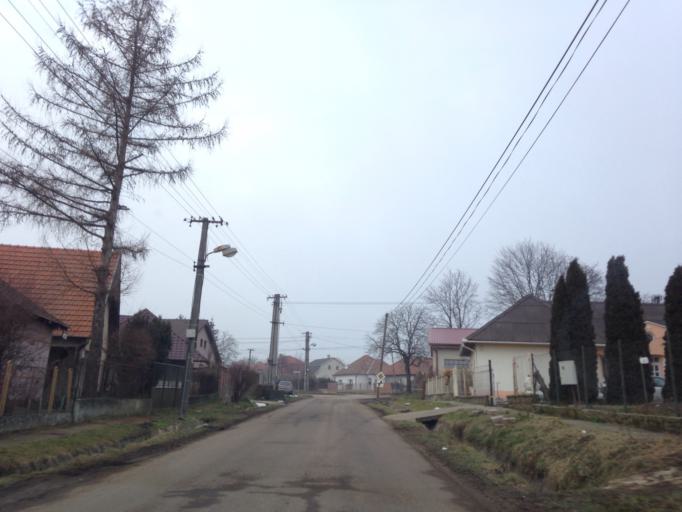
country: SK
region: Nitriansky
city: Svodin
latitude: 47.9912
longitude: 18.3921
